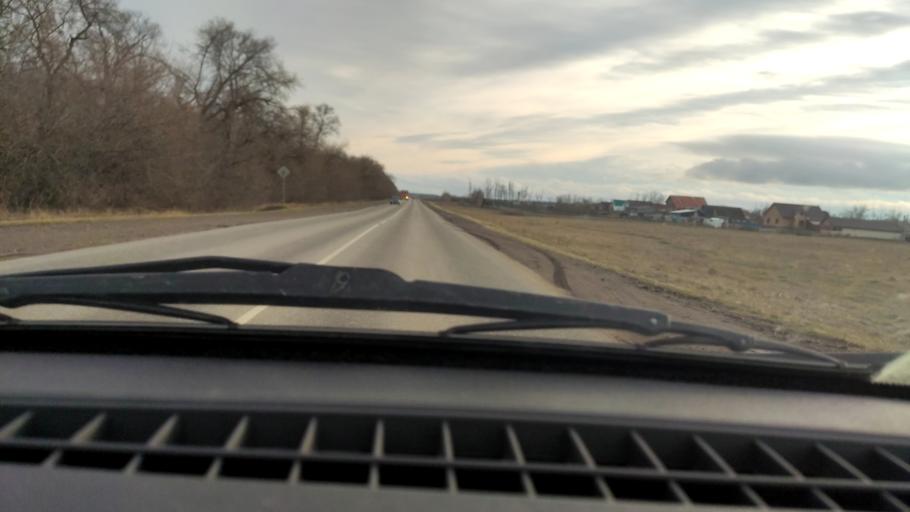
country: RU
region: Bashkortostan
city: Davlekanovo
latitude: 54.2927
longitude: 55.1228
